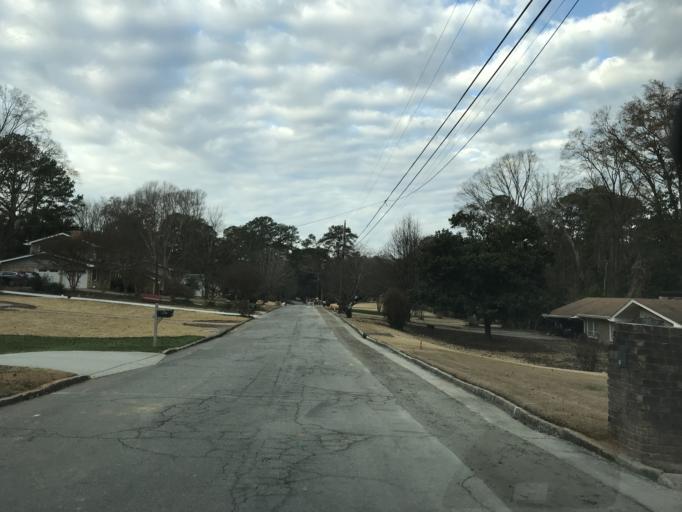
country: US
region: Georgia
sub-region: DeKalb County
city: Doraville
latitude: 33.8792
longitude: -84.2548
